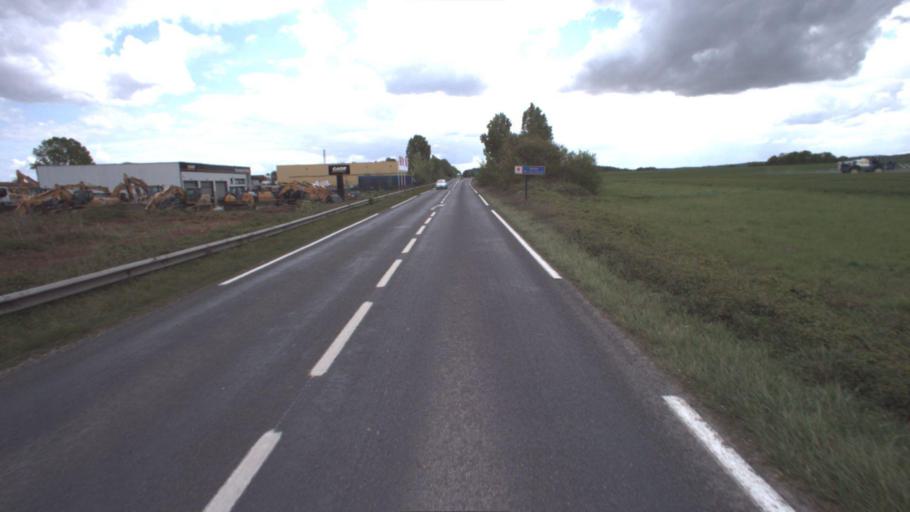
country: FR
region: Ile-de-France
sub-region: Departement de Seine-et-Marne
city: Saint-Pathus
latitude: 49.0674
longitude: 2.7730
